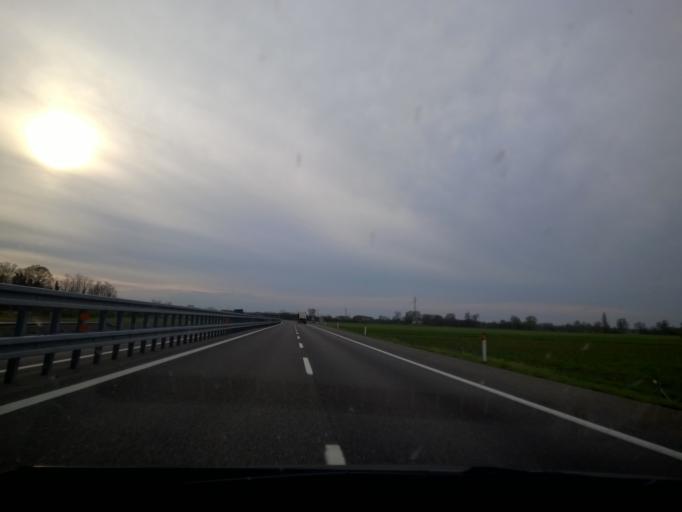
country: IT
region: Emilia-Romagna
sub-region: Provincia di Piacenza
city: Castel San Giovanni
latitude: 45.0781
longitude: 9.4354
